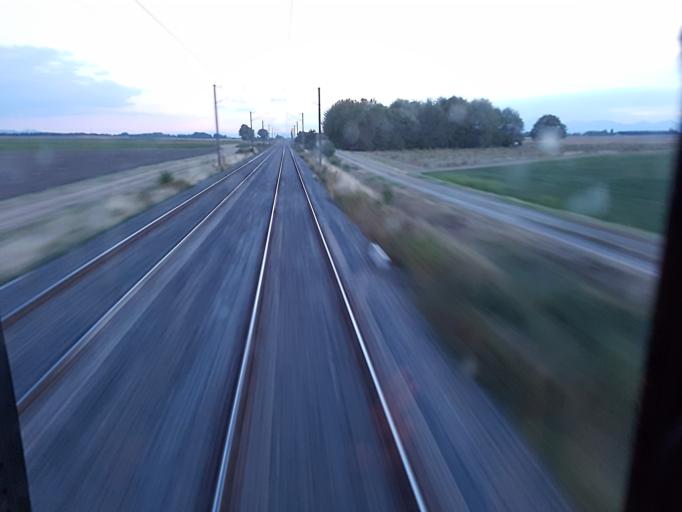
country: FR
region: Auvergne
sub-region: Departement du Puy-de-Dome
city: Ennezat
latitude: 45.9455
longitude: 3.2433
